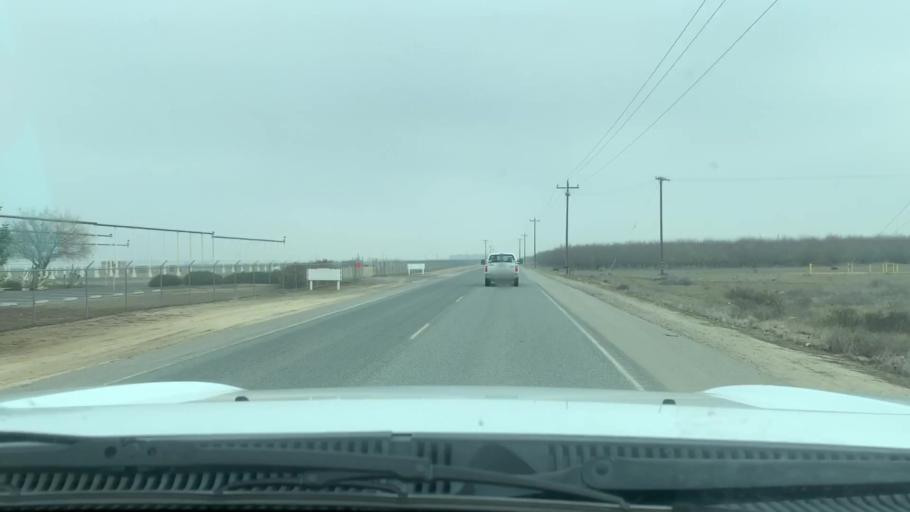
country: US
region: California
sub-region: Kern County
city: Buttonwillow
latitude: 35.5007
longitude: -119.5055
